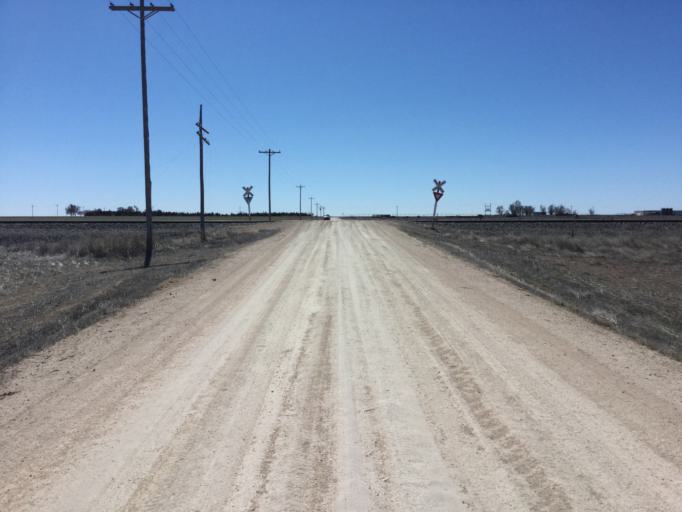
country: US
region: Kansas
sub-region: Wichita County
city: Leoti
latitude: 38.4864
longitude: -101.2752
